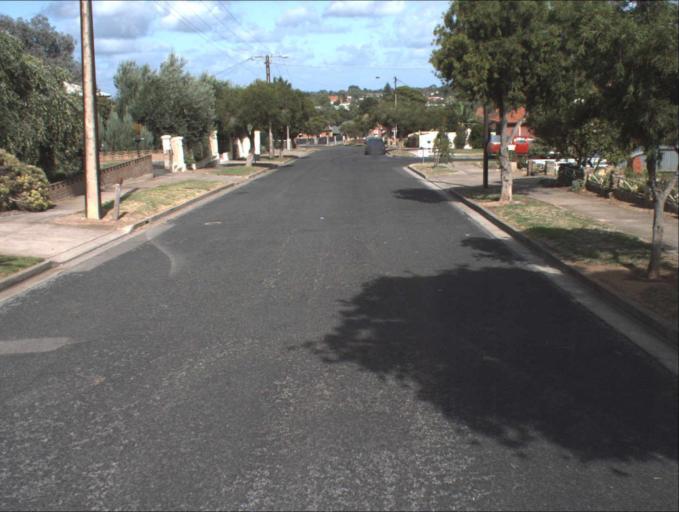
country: AU
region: South Australia
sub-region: Port Adelaide Enfield
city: Blair Athol
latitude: -34.8609
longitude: 138.5976
